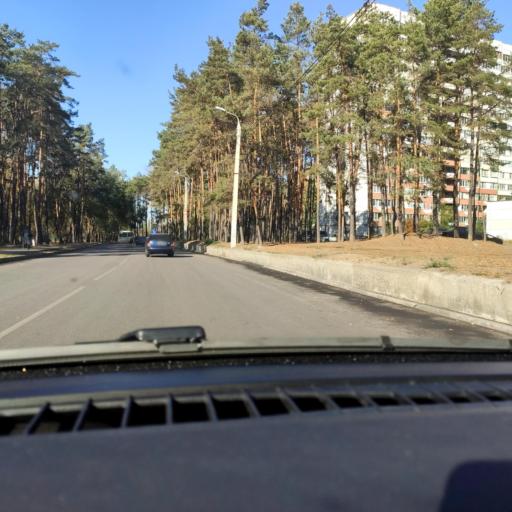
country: RU
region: Voronezj
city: Pridonskoy
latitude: 51.6842
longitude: 39.0824
